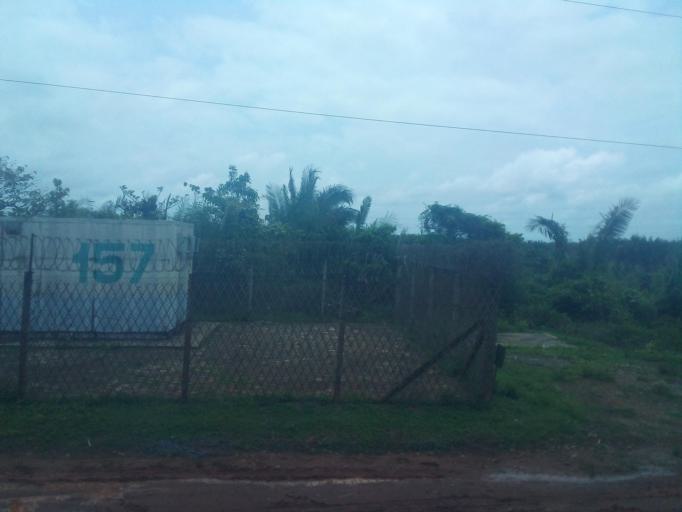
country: BR
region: Maranhao
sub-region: Vitoria Do Mearim
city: Vitoria do Mearim
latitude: -3.5796
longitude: -44.9492
